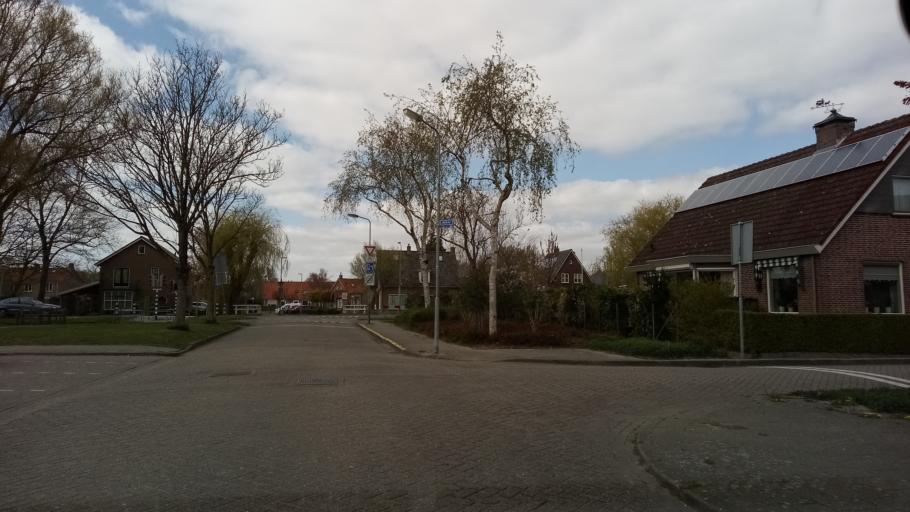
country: NL
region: North Holland
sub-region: Gemeente Langedijk
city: Broek op Langedijk
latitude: 52.6141
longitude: 4.8221
